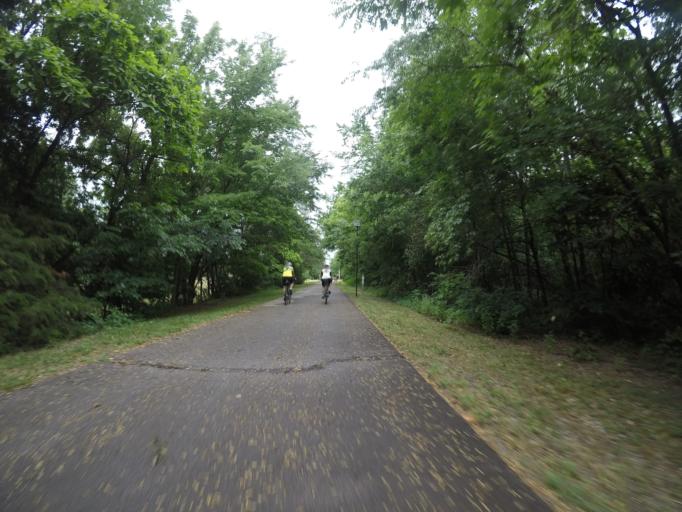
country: US
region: Kansas
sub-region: Anderson County
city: Garnett
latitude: 38.2736
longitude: -95.2420
